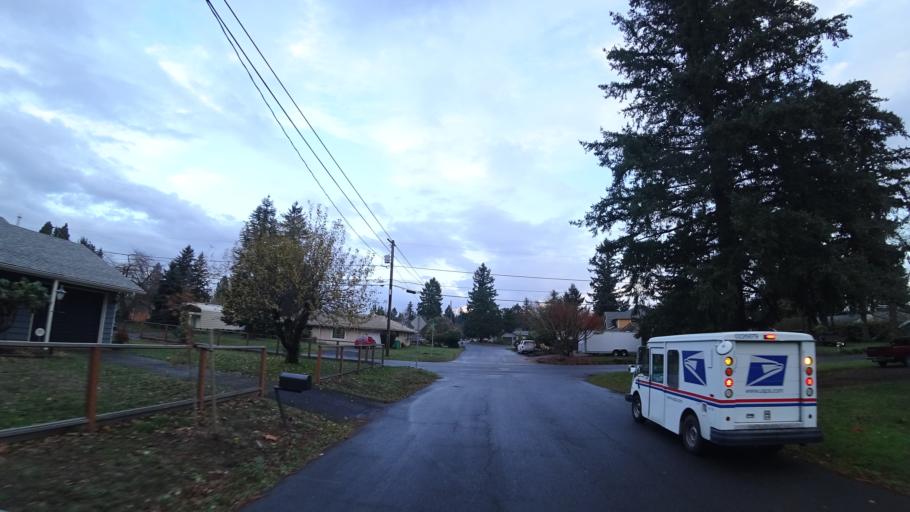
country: US
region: Oregon
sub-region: Multnomah County
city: Lents
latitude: 45.5307
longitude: -122.5342
